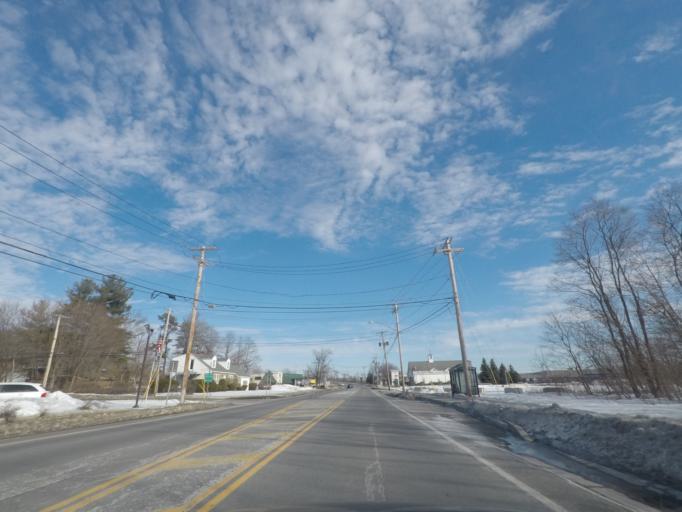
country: US
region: New York
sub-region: Schenectady County
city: Rotterdam
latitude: 42.7870
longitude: -73.9994
